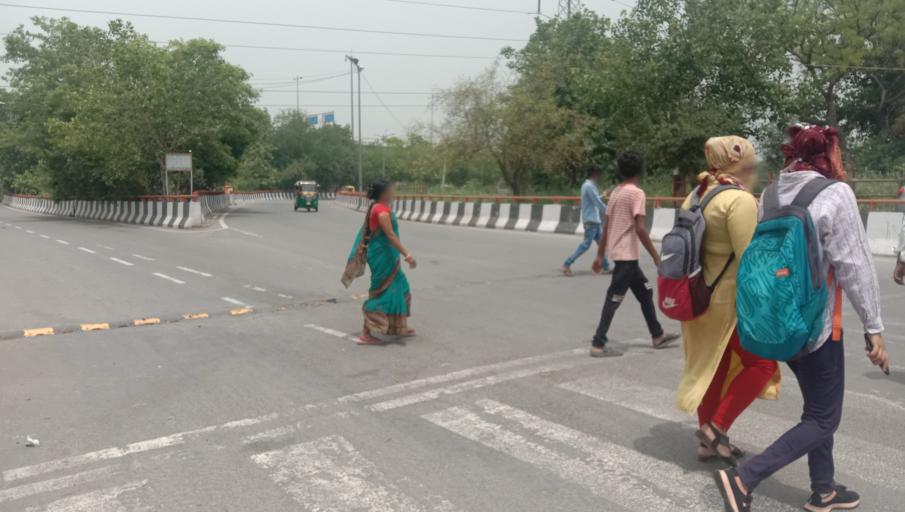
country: IN
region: NCT
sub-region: North Delhi
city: Delhi
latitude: 28.6436
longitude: 77.2704
